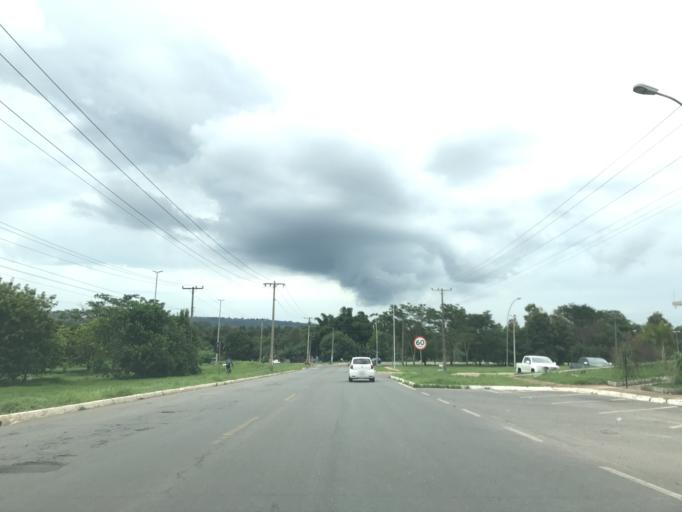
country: BR
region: Federal District
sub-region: Brasilia
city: Brasilia
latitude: -15.6549
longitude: -47.8125
